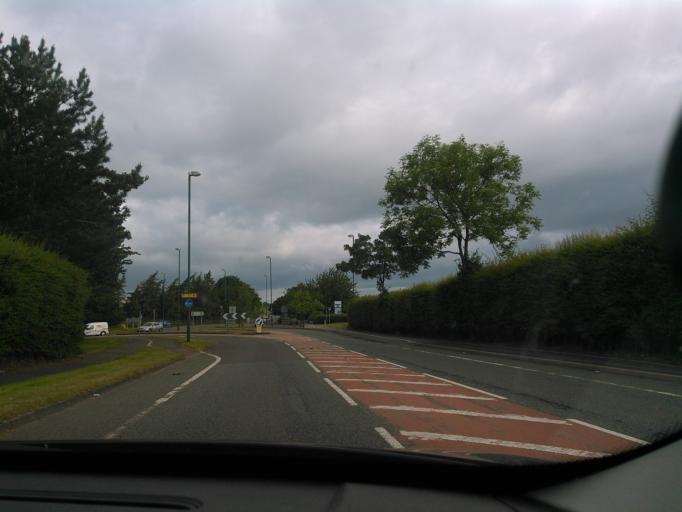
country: GB
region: England
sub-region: Shropshire
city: Shrewsbury
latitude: 52.7199
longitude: -2.7290
